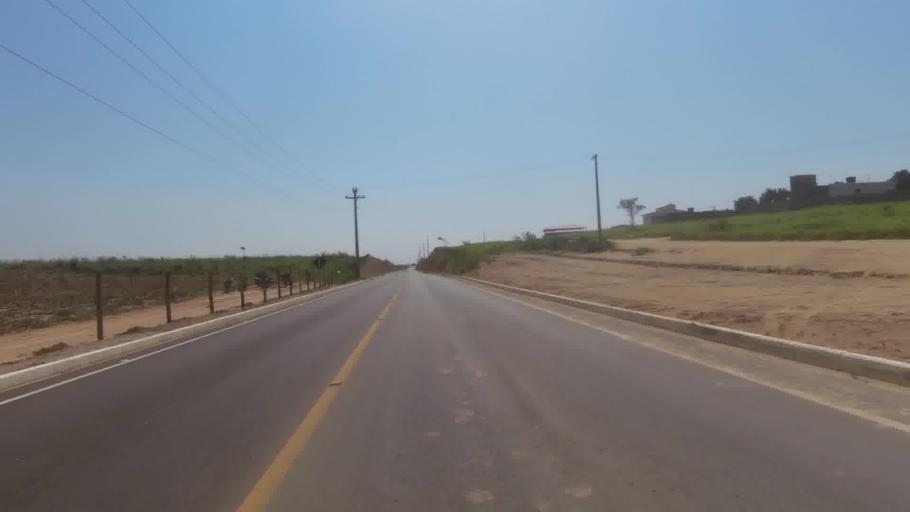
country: BR
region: Espirito Santo
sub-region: Marataizes
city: Marataizes
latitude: -21.0443
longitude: -40.8443
